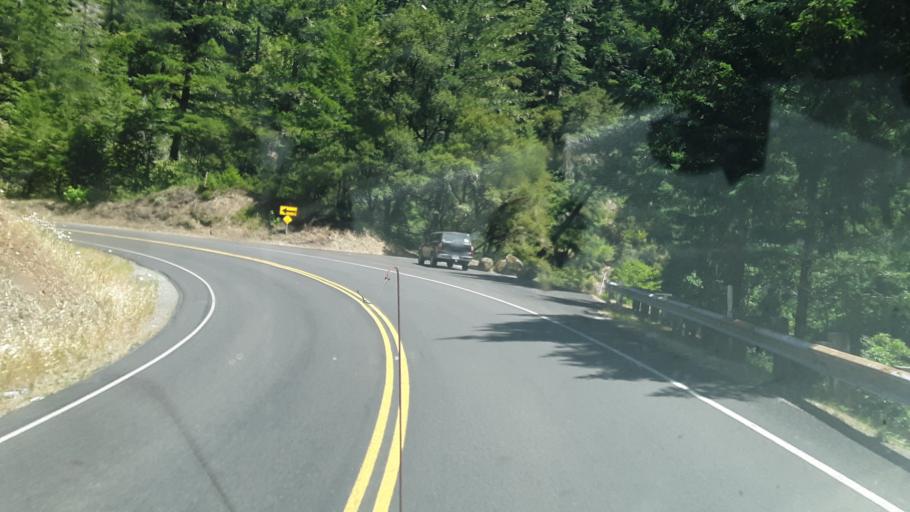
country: US
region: Oregon
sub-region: Josephine County
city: Cave Junction
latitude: 41.8783
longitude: -123.8283
